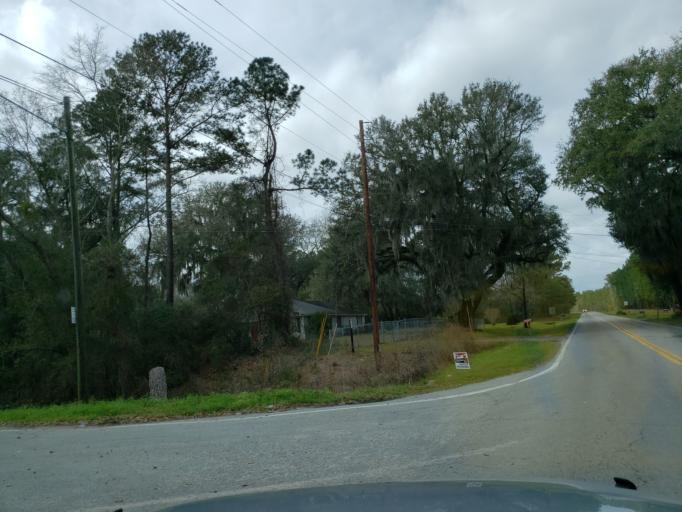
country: US
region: Georgia
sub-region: Chatham County
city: Pooler
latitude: 32.0491
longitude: -81.2862
